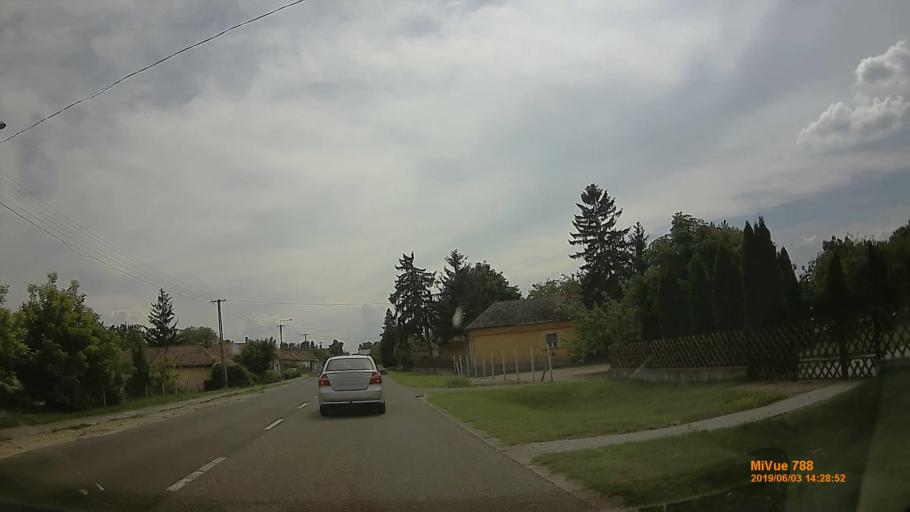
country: HU
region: Bacs-Kiskun
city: Tiszakecske
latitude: 46.9753
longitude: 20.1120
